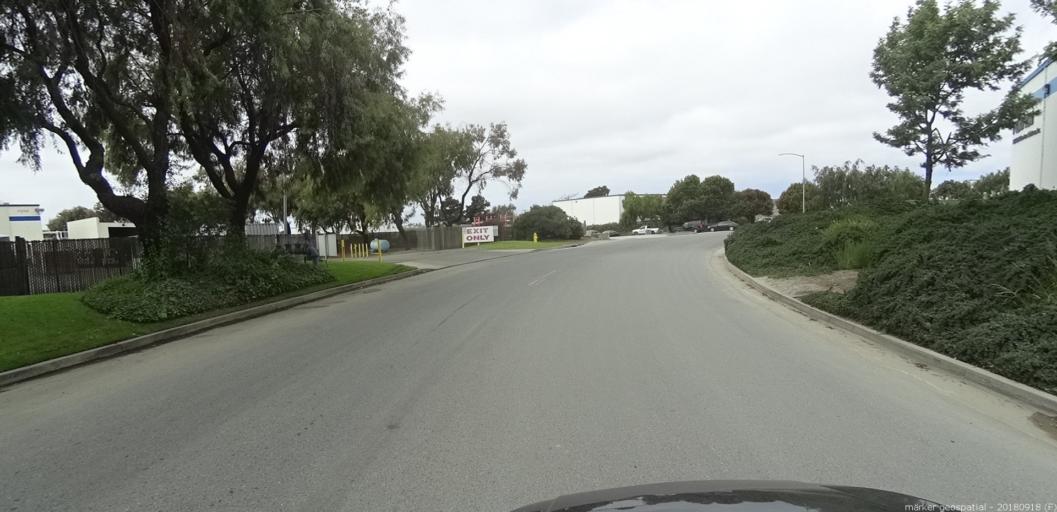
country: US
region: California
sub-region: Monterey County
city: Castroville
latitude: 36.7540
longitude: -121.7402
